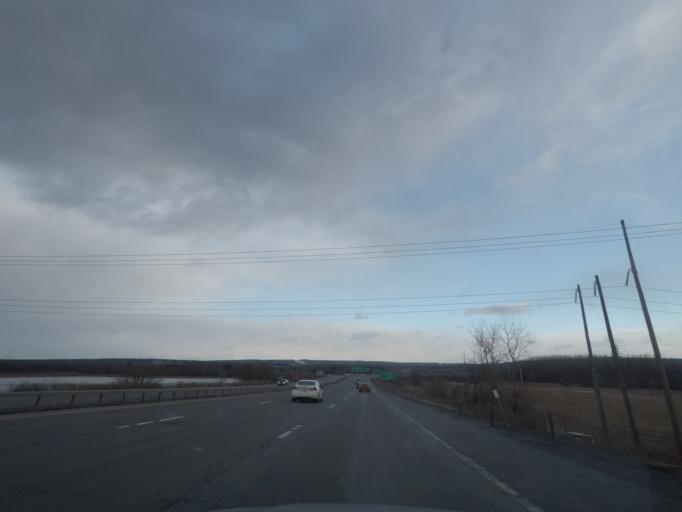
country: US
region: New York
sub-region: Oneida County
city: Utica
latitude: 43.1139
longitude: -75.2351
